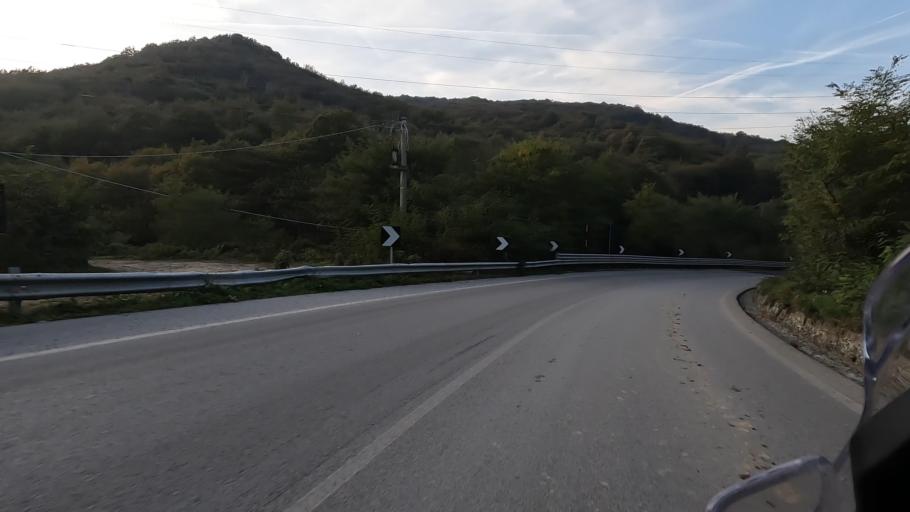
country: IT
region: Liguria
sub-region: Provincia di Savona
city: Osteria dei Cacciatori-Stella
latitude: 44.4481
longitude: 8.4771
